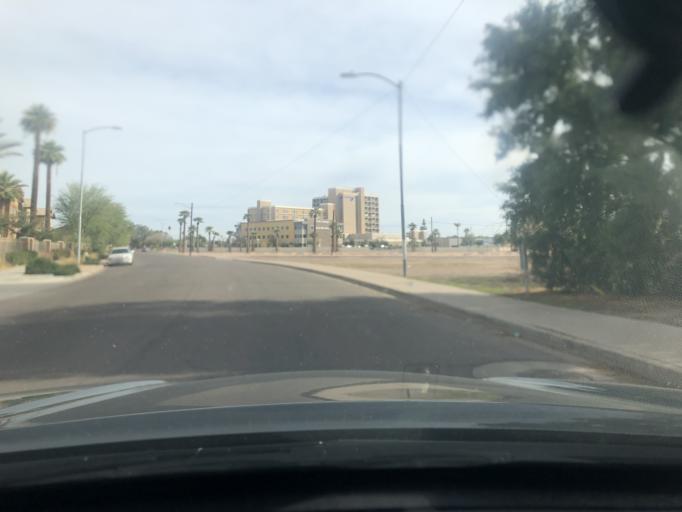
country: US
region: Arizona
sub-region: Maricopa County
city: Phoenix
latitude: 33.4548
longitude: -112.0466
